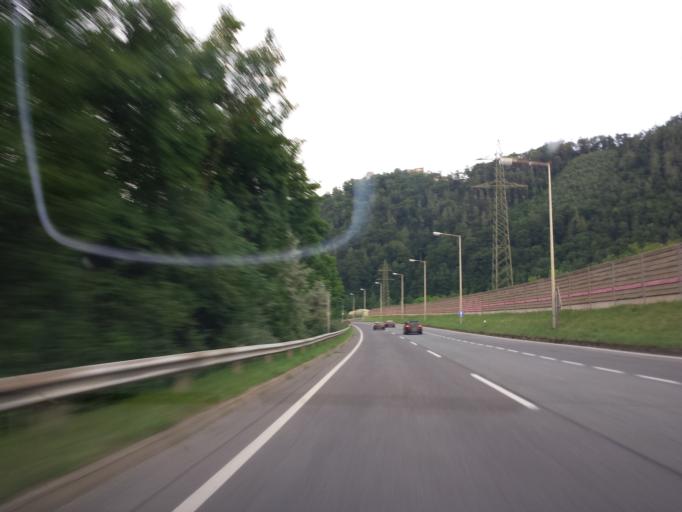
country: AT
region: Styria
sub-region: Graz Stadt
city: Goesting
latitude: 47.1104
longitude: 15.3762
